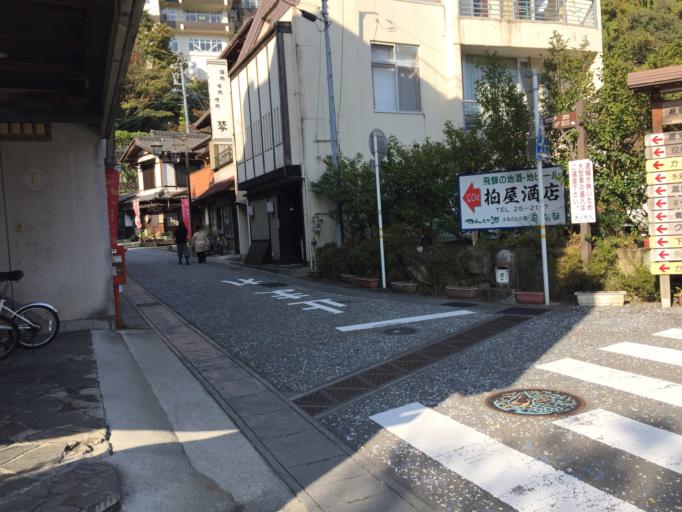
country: JP
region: Gifu
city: Gujo
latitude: 35.8089
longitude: 137.2441
